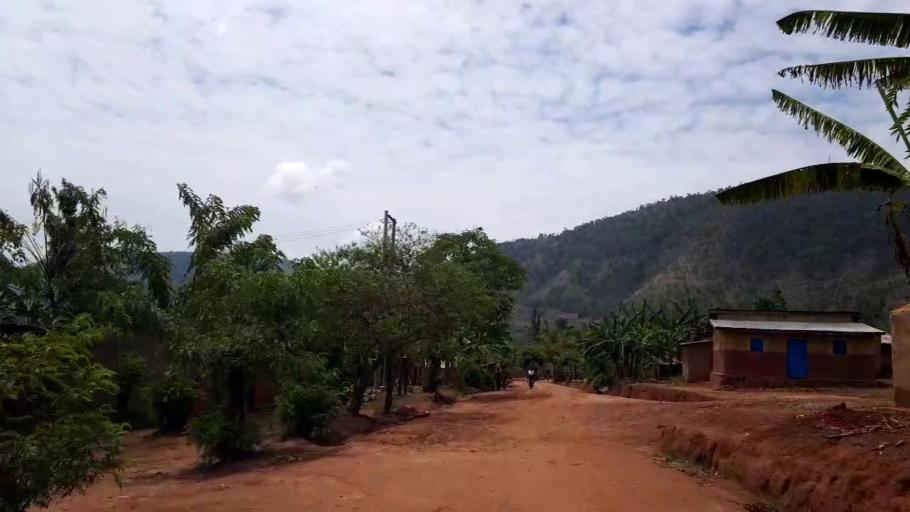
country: RW
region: Northern Province
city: Byumba
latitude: -1.4958
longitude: 30.1948
